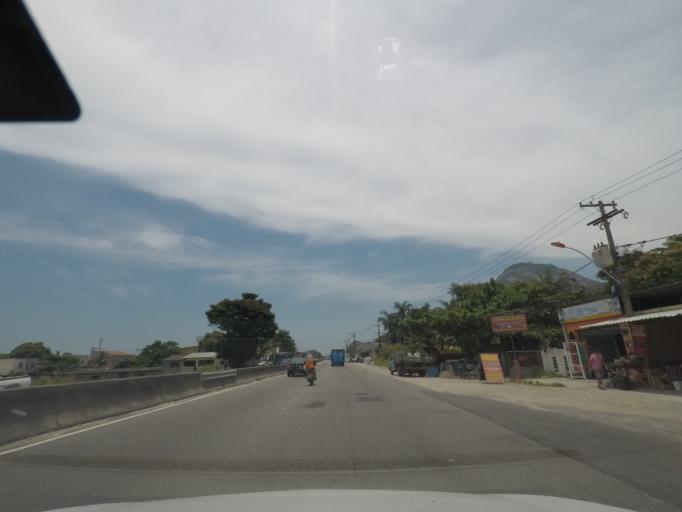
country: BR
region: Rio de Janeiro
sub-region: Marica
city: Marica
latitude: -22.9329
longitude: -42.8909
